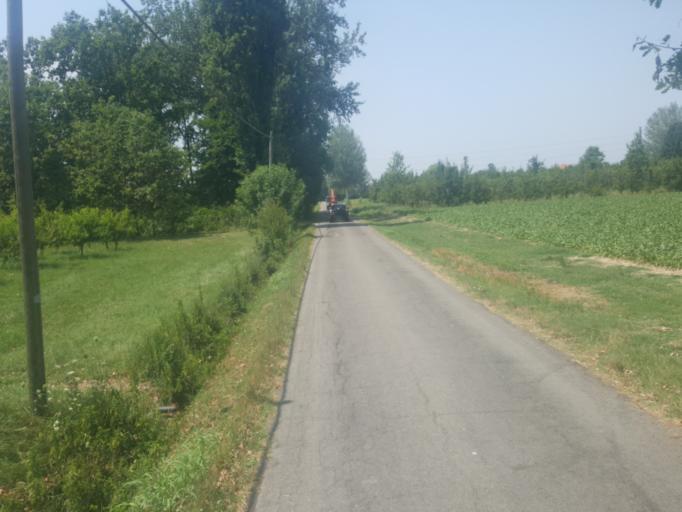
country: IT
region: Emilia-Romagna
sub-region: Provincia di Modena
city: Gaggio
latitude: 44.6446
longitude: 11.0062
